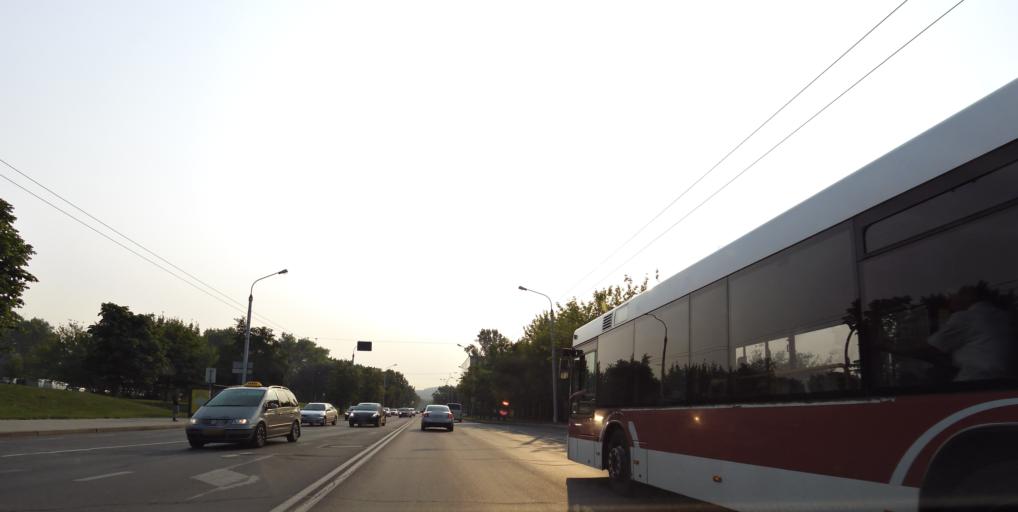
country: LT
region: Vilnius County
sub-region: Vilnius
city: Vilnius
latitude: 54.6948
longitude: 25.2889
